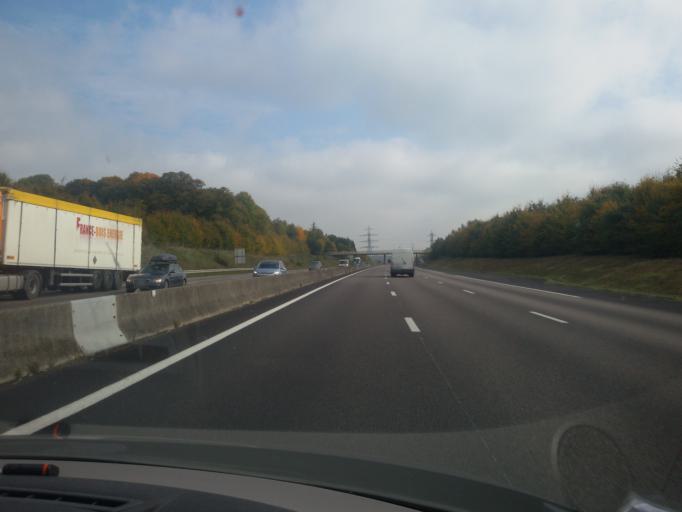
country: FR
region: Haute-Normandie
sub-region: Departement de l'Eure
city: Saint-Ouen-de-Thouberville
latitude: 49.3485
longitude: 0.9042
